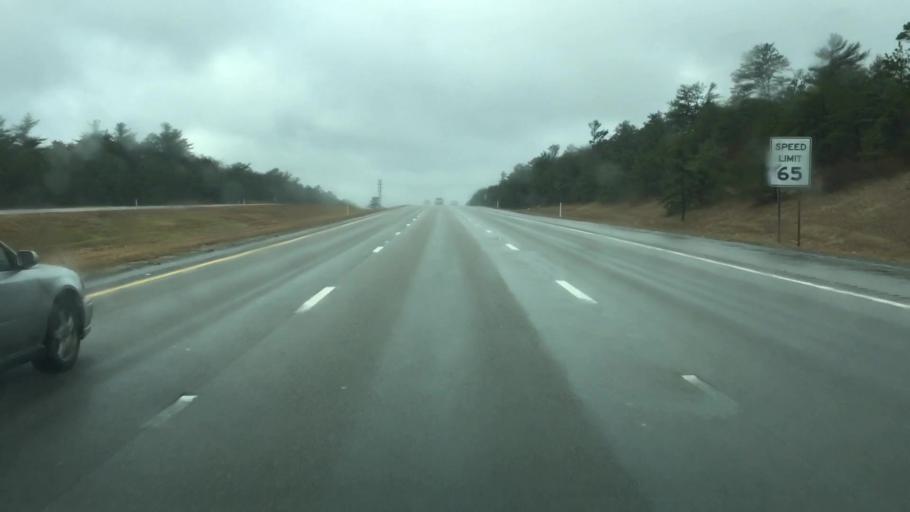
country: US
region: Massachusetts
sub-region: Plymouth County
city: White Island Shores
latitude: 41.7728
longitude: -70.6412
